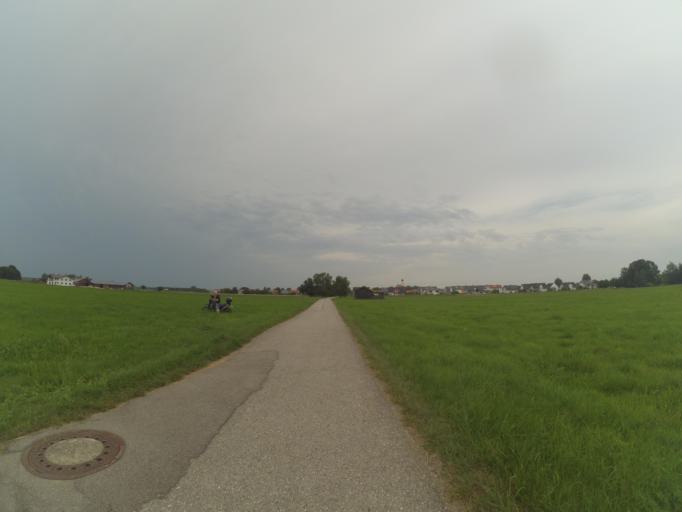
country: DE
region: Bavaria
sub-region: Swabia
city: Jengen
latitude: 48.0098
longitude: 10.7194
